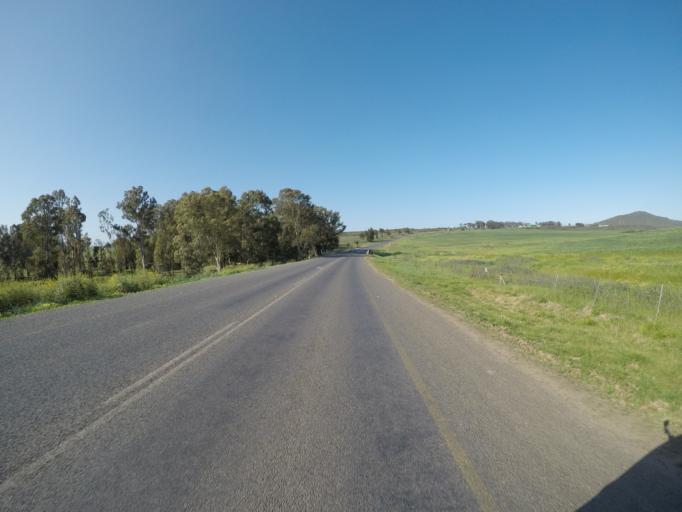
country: ZA
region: Western Cape
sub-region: City of Cape Town
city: Kraaifontein
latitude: -33.7654
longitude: 18.7614
